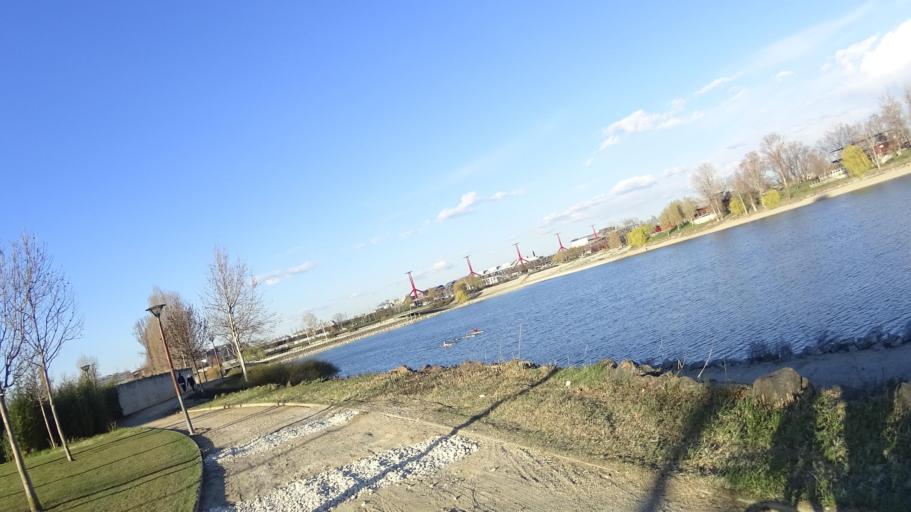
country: HU
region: Budapest
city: Budapest IX. keruelet
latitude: 47.4638
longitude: 19.0590
